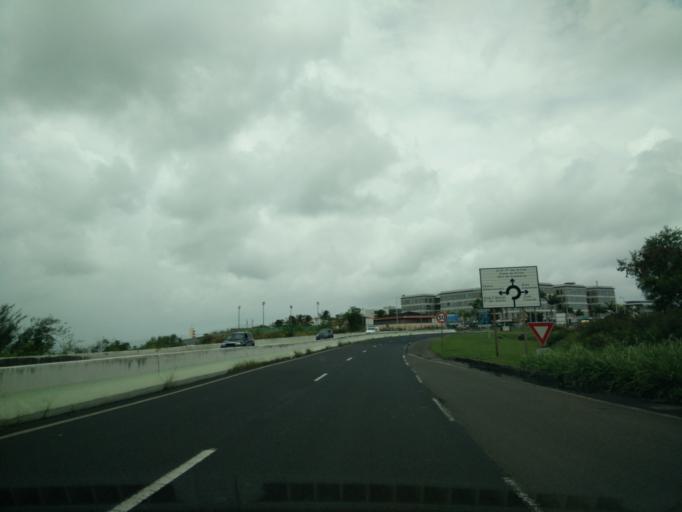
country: MQ
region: Martinique
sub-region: Martinique
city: Fort-de-France
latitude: 14.6061
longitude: -61.0422
